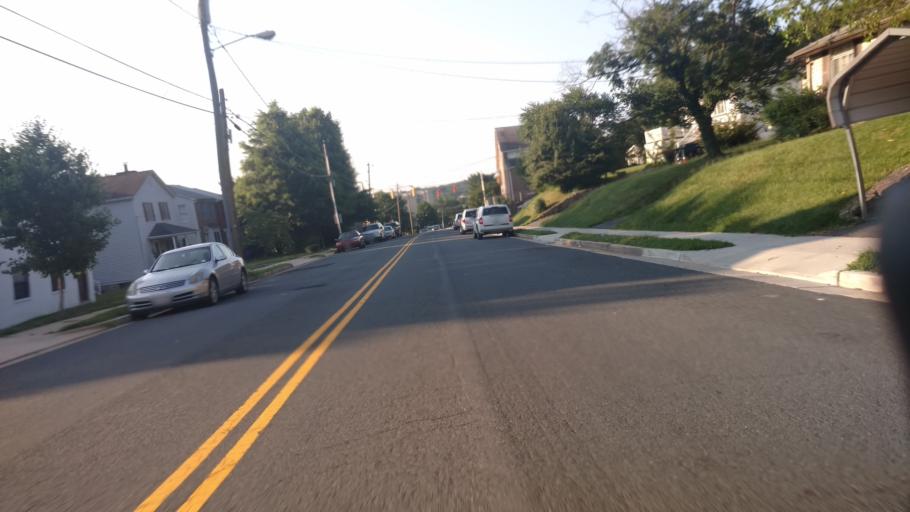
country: US
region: Virginia
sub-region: Arlington County
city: Arlington
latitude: 38.8507
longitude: -77.0862
